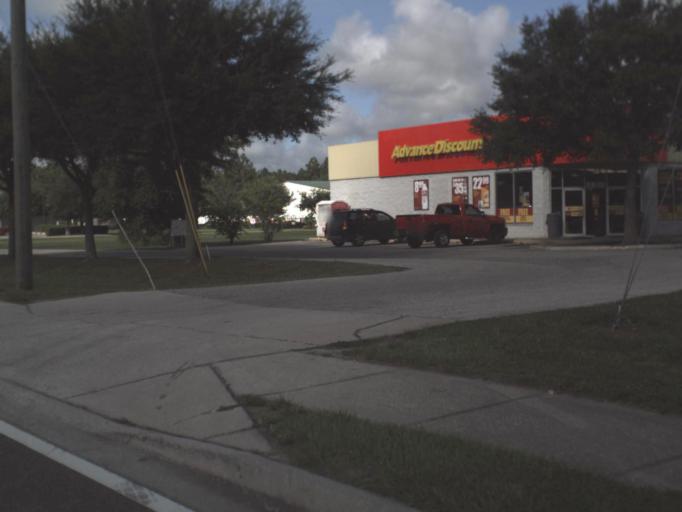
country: US
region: Florida
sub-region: Pasco County
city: Land O' Lakes
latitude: 28.2139
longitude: -82.4611
